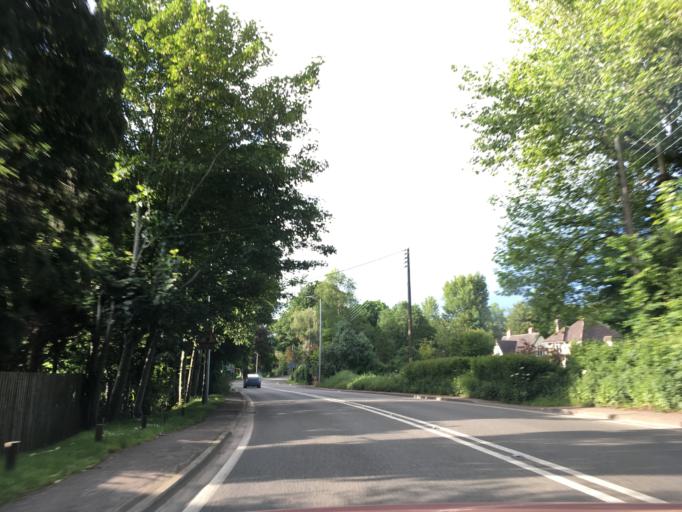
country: GB
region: England
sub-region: North Somerset
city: Winscombe
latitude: 51.3101
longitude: -2.8250
